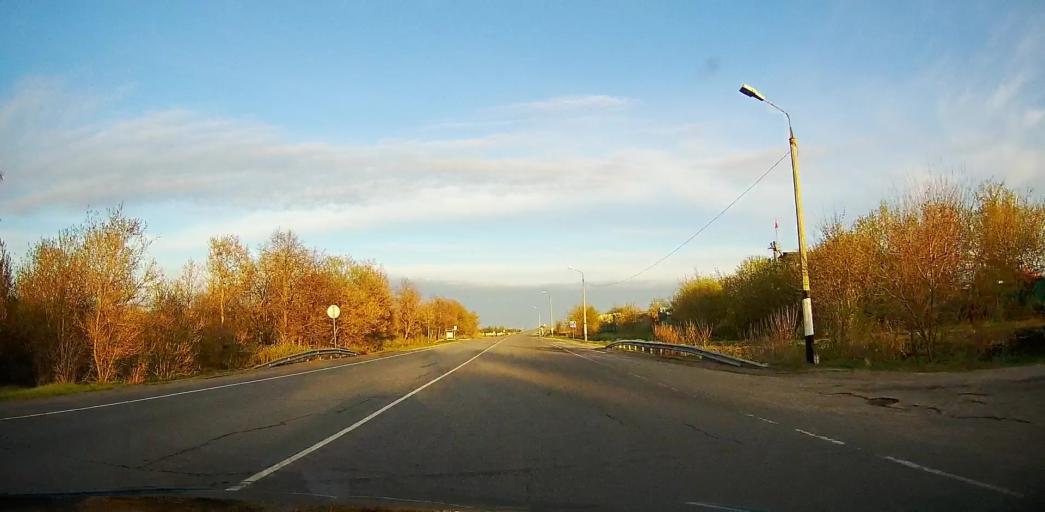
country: RU
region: Moskovskaya
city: Troitskoye
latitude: 55.2209
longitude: 38.5803
